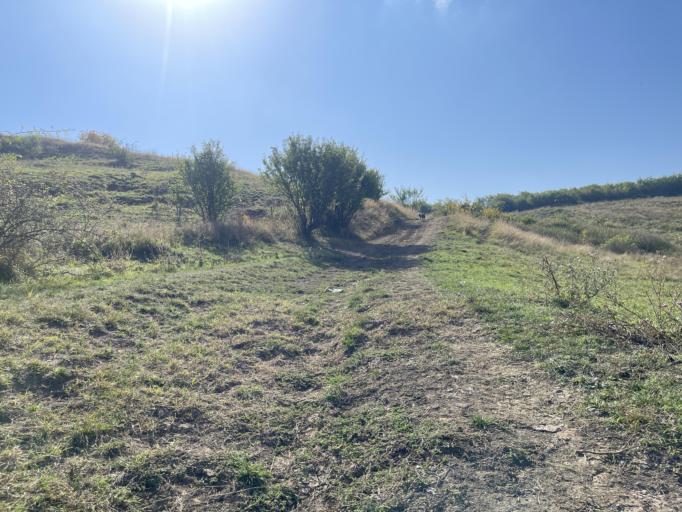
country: RO
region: Iasi
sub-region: Comuna Dumesti
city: Pausesti
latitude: 47.1596
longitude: 27.3143
